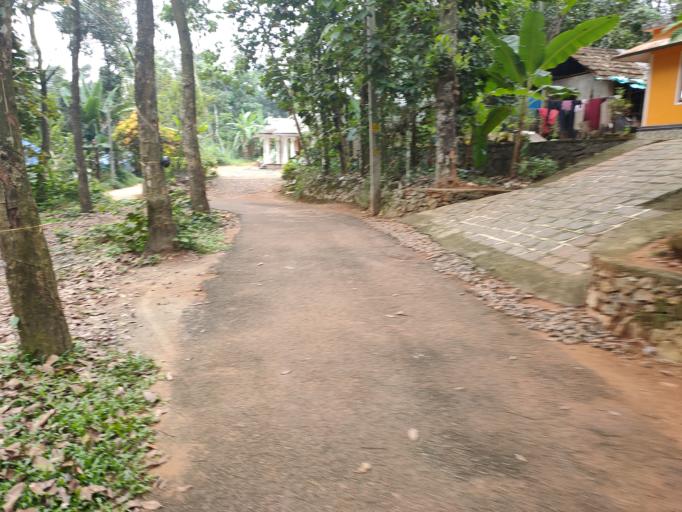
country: IN
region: Kerala
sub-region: Ernakulam
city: Kotamangalam
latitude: 10.0007
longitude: 76.6400
